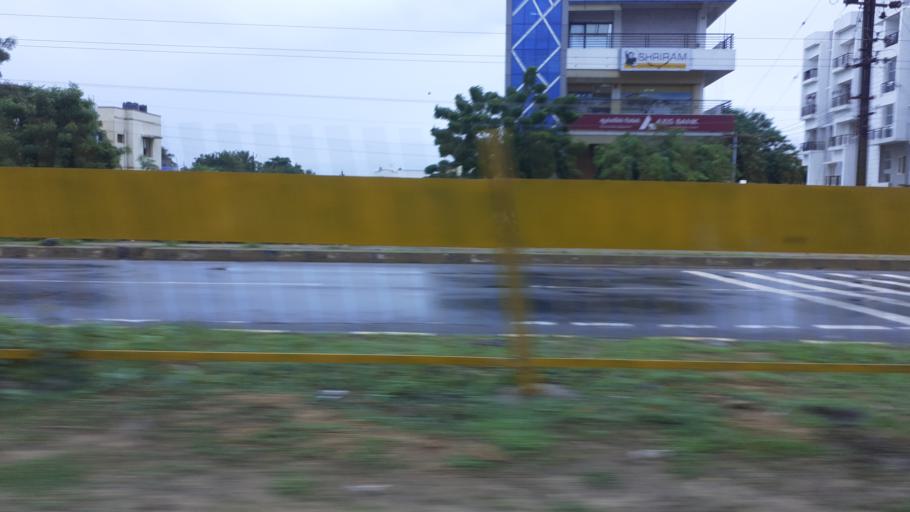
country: IN
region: Tamil Nadu
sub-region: Tirunelveli Kattabo
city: Tirunelveli
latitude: 8.7138
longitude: 77.7737
